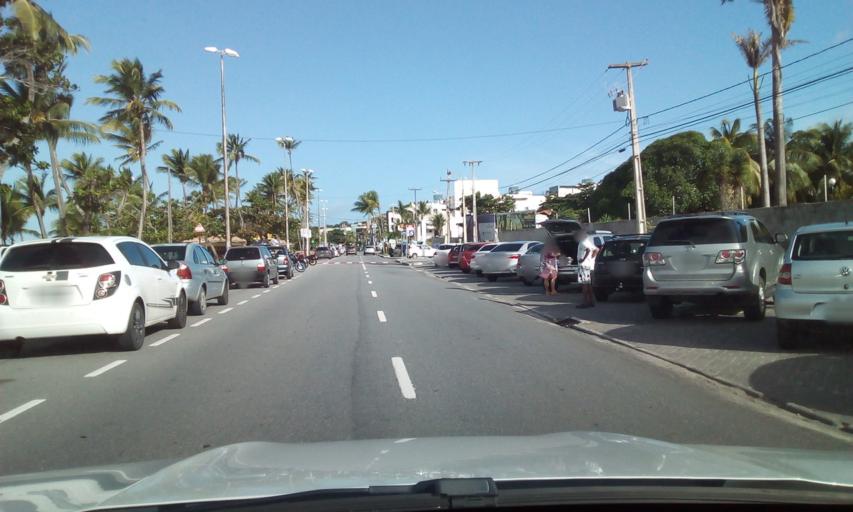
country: BR
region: Paraiba
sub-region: Joao Pessoa
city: Joao Pessoa
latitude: -7.1306
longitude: -34.8223
